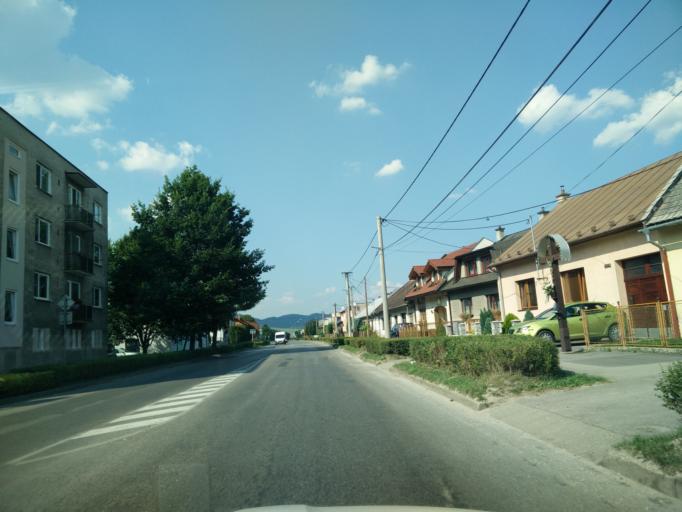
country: SK
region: Zilinsky
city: Rajec
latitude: 49.0906
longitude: 18.6392
